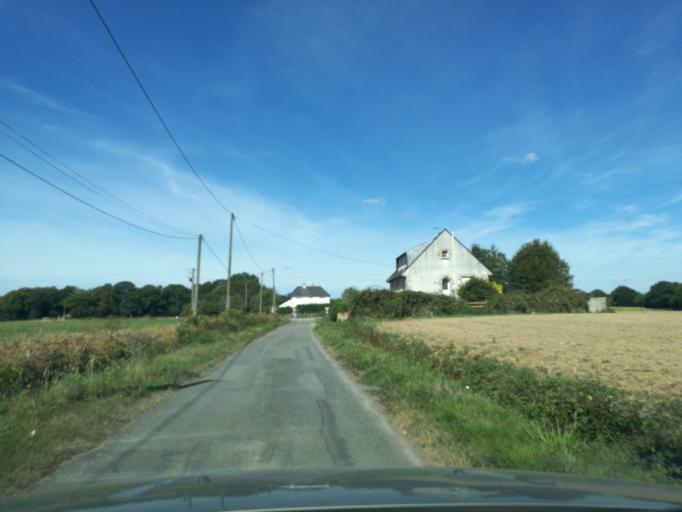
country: FR
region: Brittany
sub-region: Departement d'Ille-et-Vilaine
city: Montfort-sur-Meu
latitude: 48.1366
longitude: -1.9299
